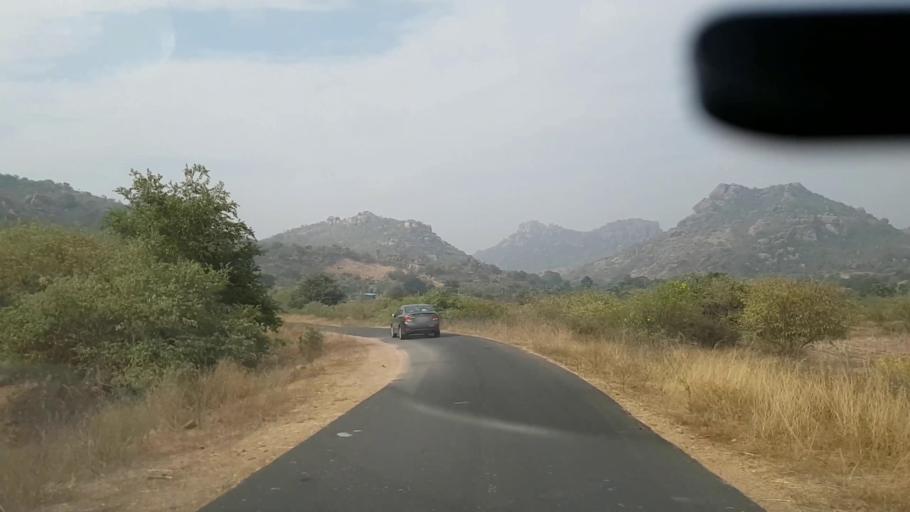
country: IN
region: Telangana
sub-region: Rangareddi
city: Ghatkesar
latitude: 17.1728
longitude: 78.8180
